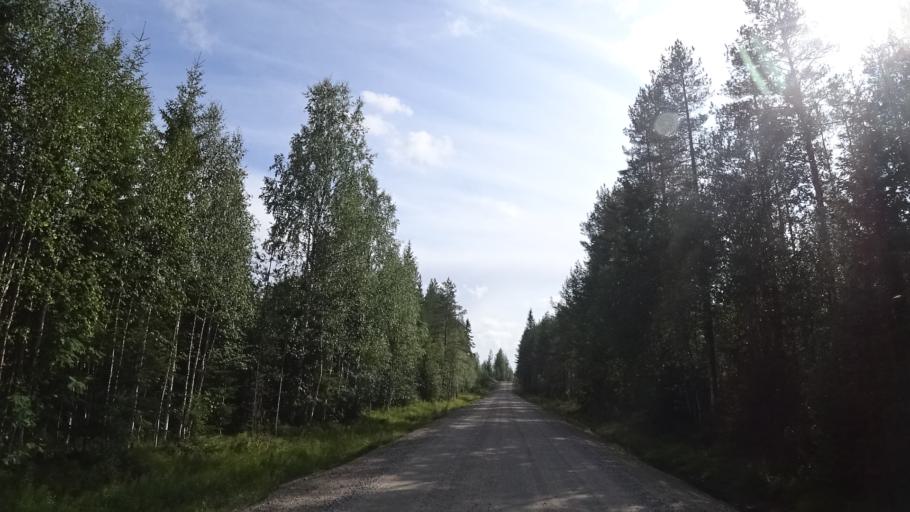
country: FI
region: North Karelia
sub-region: Pielisen Karjala
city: Lieksa
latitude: 63.5906
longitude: 30.1355
